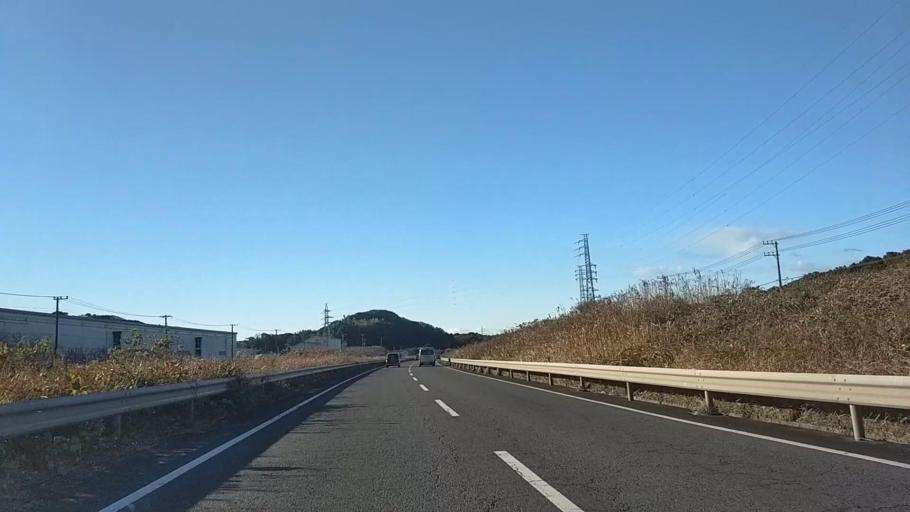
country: JP
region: Chiba
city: Kisarazu
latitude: 35.3600
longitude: 139.9106
